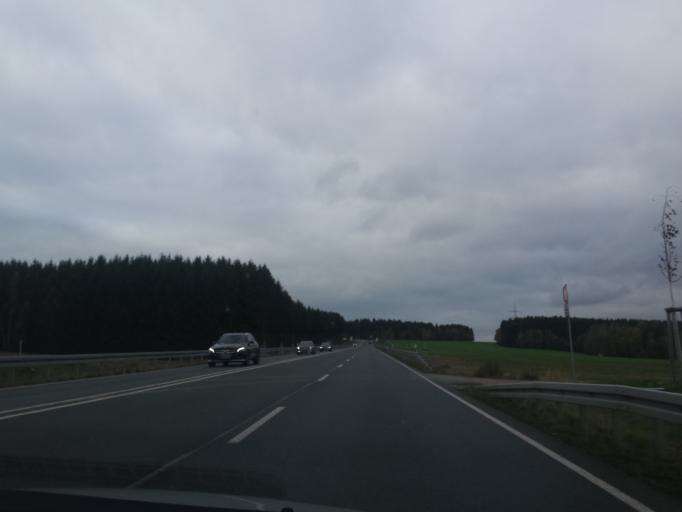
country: DE
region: Saxony
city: Dorfchemnitz
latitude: 50.6655
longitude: 12.8088
